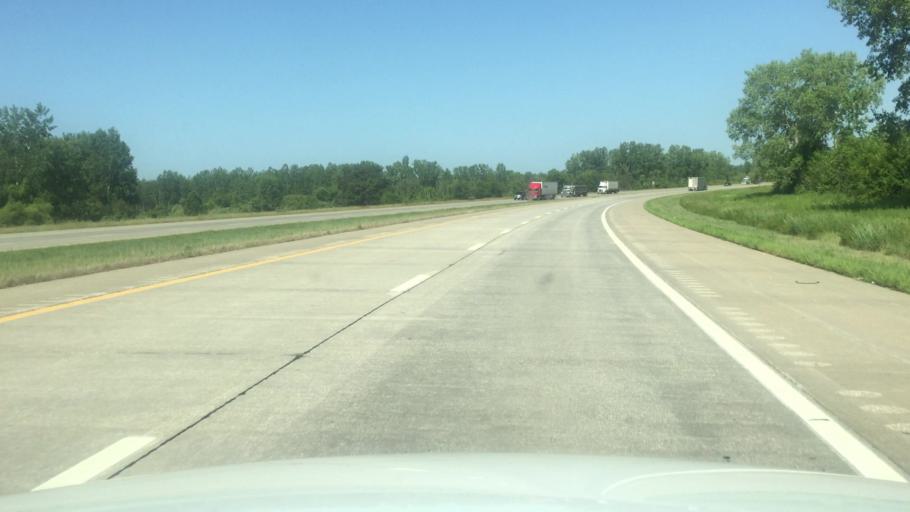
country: US
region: Kansas
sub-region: Doniphan County
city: Wathena
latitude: 39.7407
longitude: -94.9140
